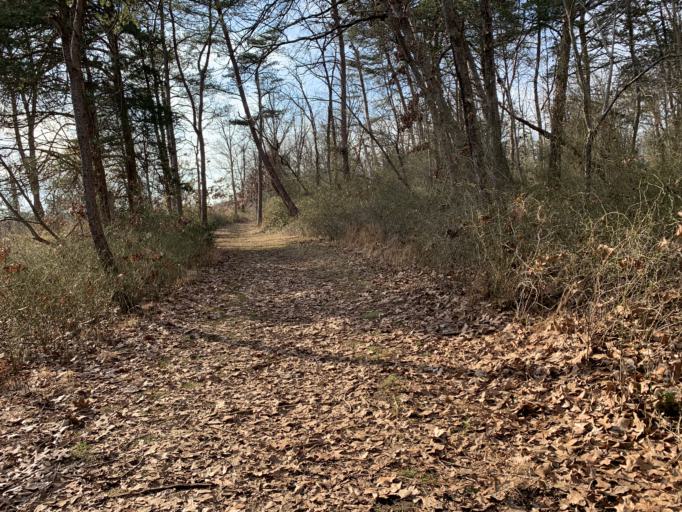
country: US
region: Pennsylvania
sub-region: Chester County
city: Malvern
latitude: 40.0106
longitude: -75.5207
